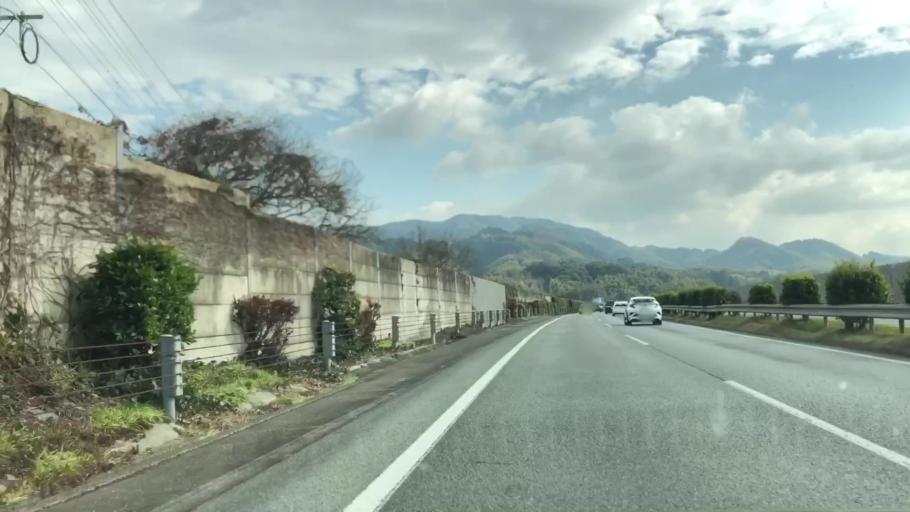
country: JP
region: Fukuoka
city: Setakamachi-takayanagi
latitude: 33.1169
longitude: 130.5267
